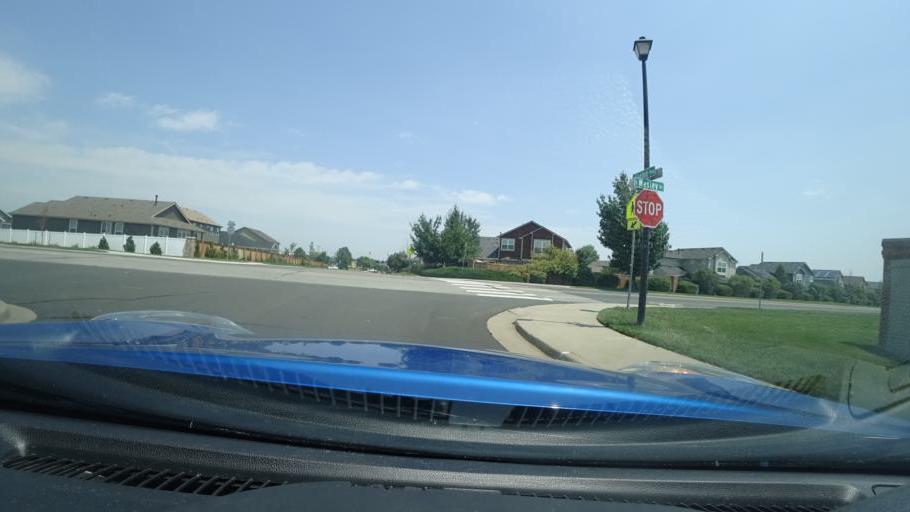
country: US
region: Colorado
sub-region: Adams County
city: Aurora
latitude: 39.6761
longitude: -104.7653
